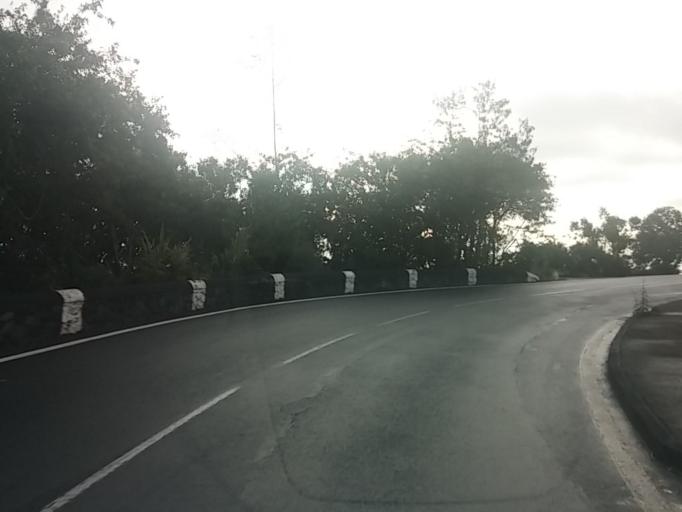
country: RE
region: Reunion
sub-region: Reunion
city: Saint-Denis
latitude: -20.8990
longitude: 55.4169
